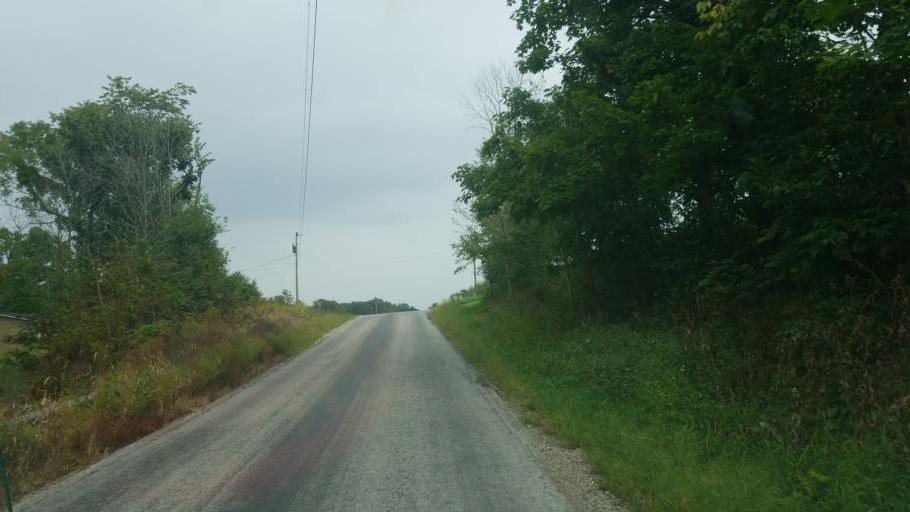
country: US
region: Ohio
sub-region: Wayne County
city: Creston
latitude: 40.9592
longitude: -81.9455
